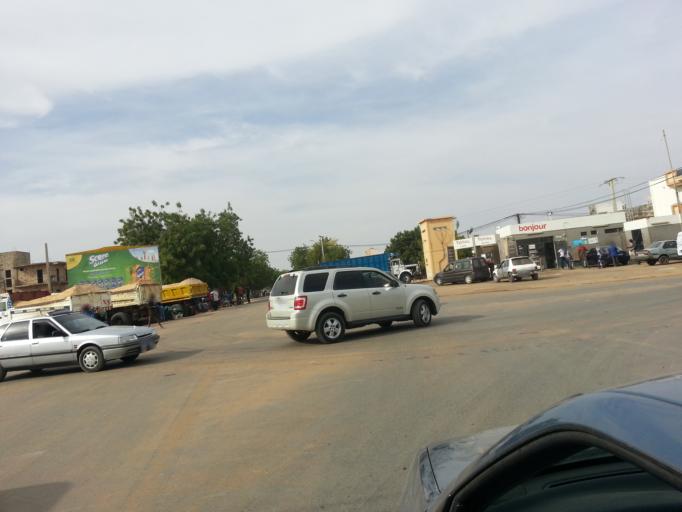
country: SN
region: Diourbel
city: Touba
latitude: 14.8662
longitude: -15.8612
